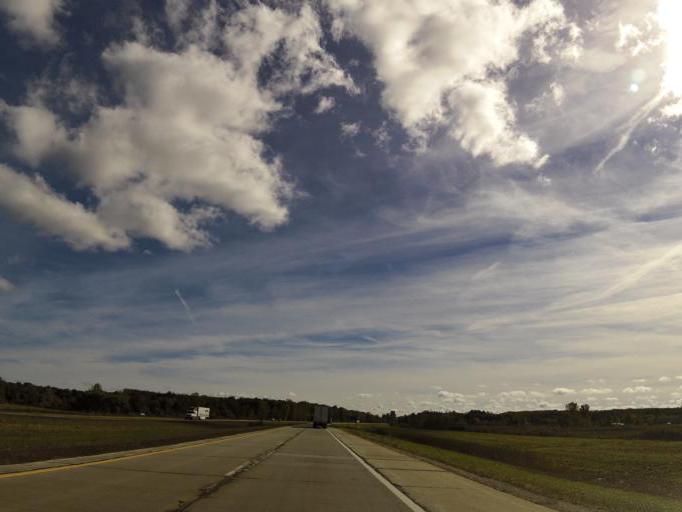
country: US
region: Michigan
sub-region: Saint Clair County
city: Capac
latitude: 42.9872
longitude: -82.8682
